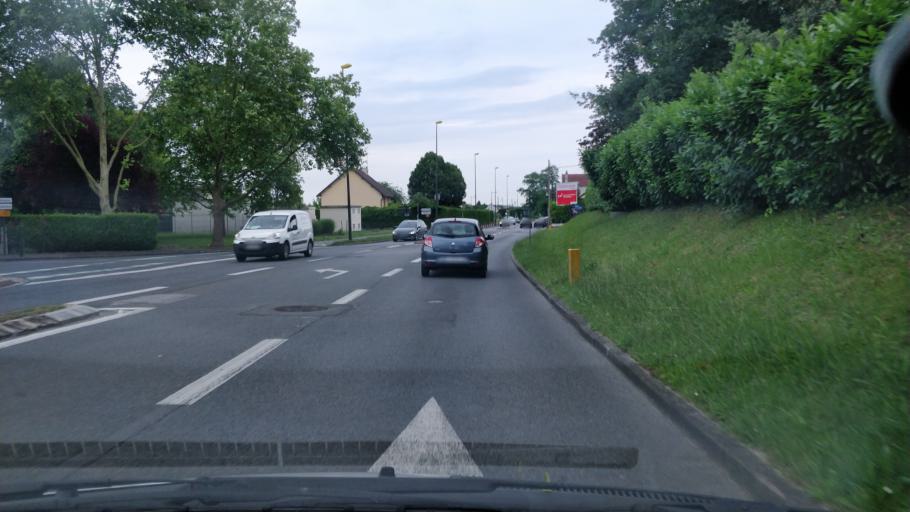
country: FR
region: Ile-de-France
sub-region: Departement de Seine-et-Marne
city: Chelles
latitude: 48.8895
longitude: 2.6040
